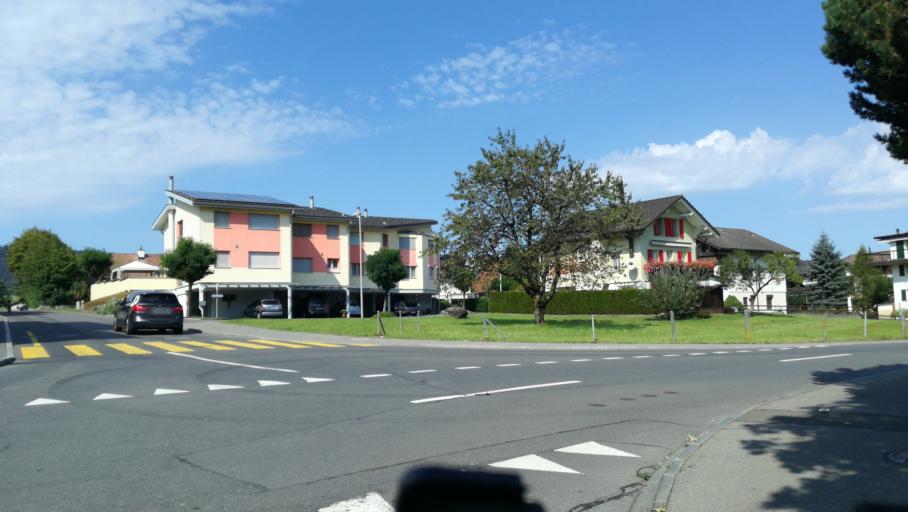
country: CH
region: Zug
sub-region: Zug
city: Unterageri
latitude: 47.1357
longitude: 8.5770
